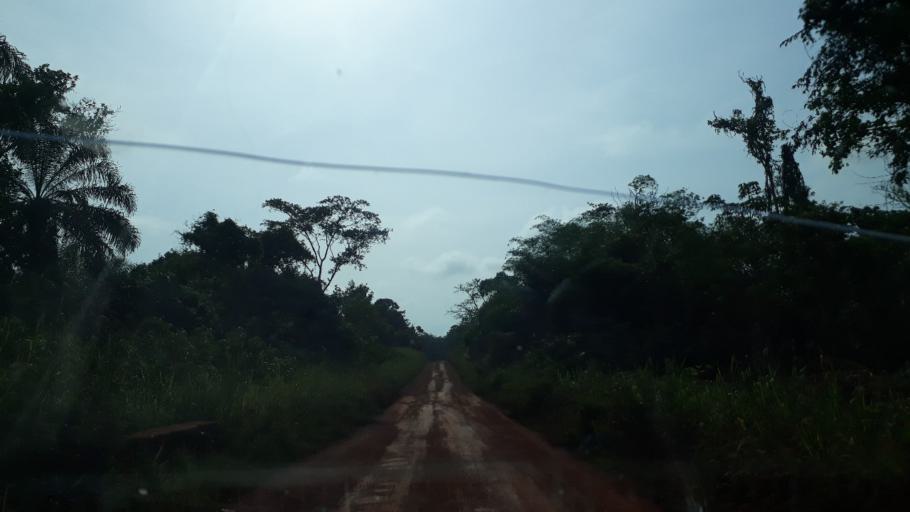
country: CD
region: Eastern Province
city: Wamba
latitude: 1.4059
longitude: 27.6483
